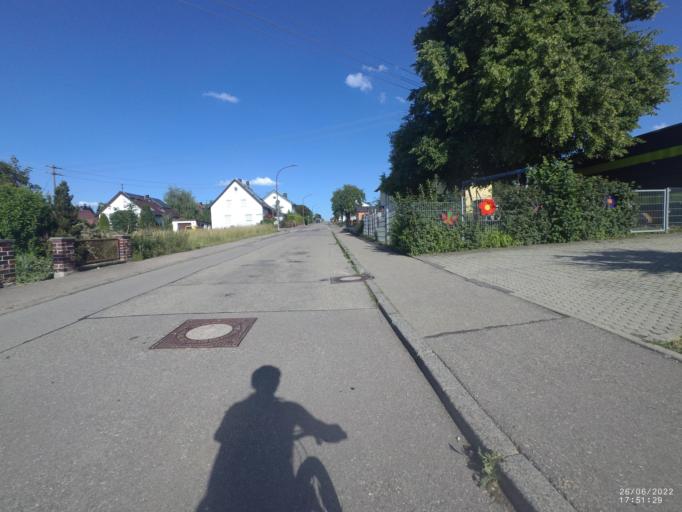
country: DE
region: Baden-Wuerttemberg
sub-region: Regierungsbezirk Stuttgart
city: Bohmenkirch
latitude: 48.6420
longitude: 9.9629
